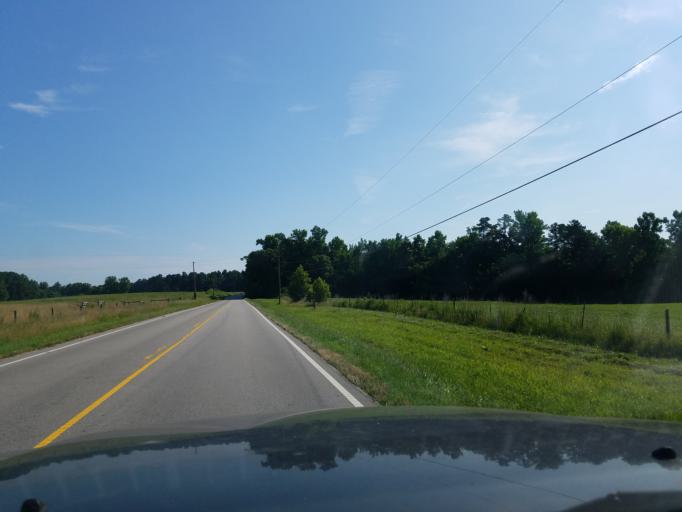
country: US
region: North Carolina
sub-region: Granville County
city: Butner
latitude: 36.1687
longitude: -78.7594
